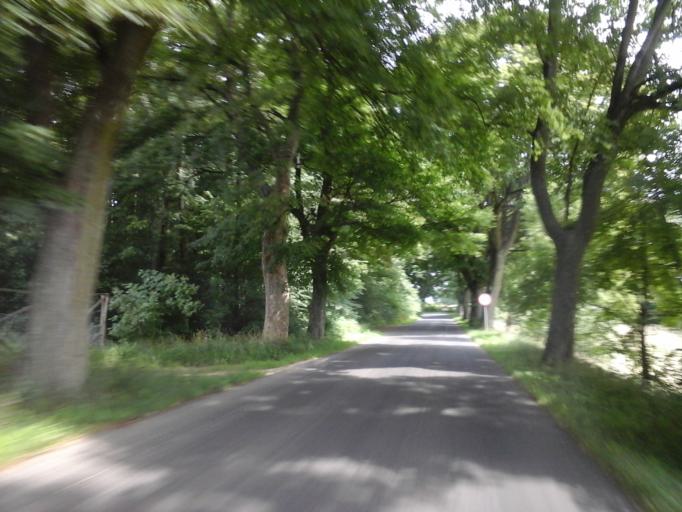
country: PL
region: West Pomeranian Voivodeship
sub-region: Powiat choszczenski
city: Recz
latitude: 53.2462
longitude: 15.6076
